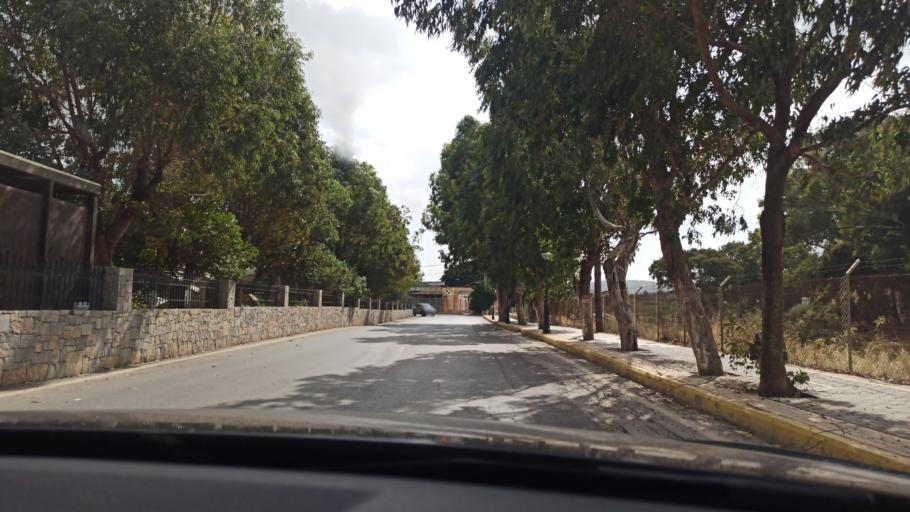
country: GR
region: Crete
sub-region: Nomos Irakleiou
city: Gazi
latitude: 35.3379
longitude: 25.0562
